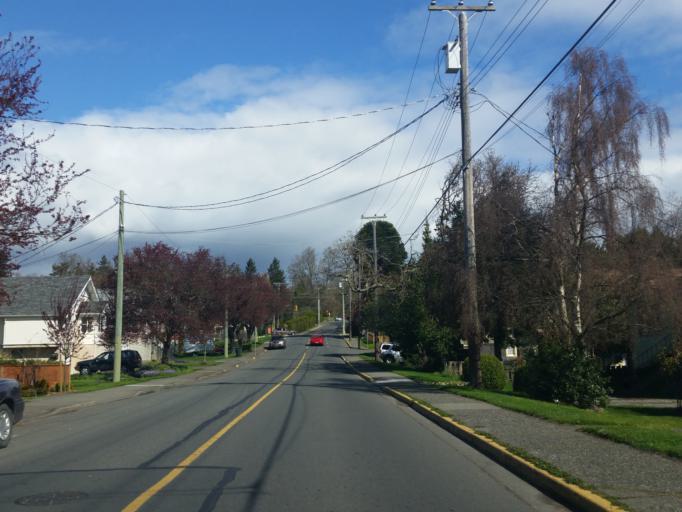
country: CA
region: British Columbia
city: Victoria
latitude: 48.4281
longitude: -123.4073
